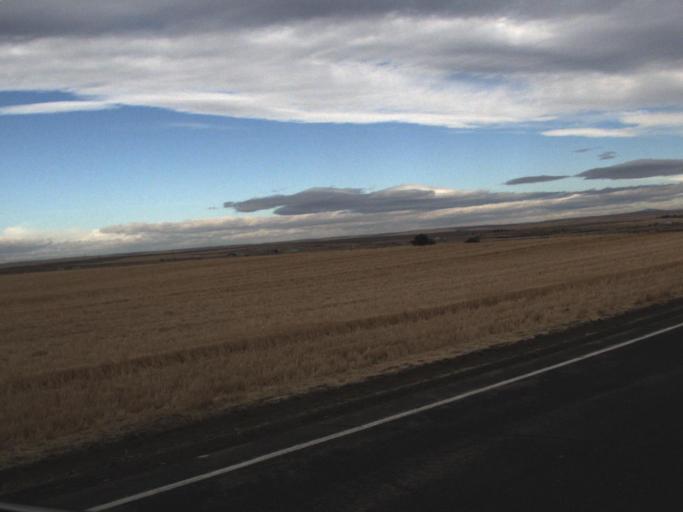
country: US
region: Washington
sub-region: Okanogan County
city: Coulee Dam
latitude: 47.7383
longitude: -118.7219
